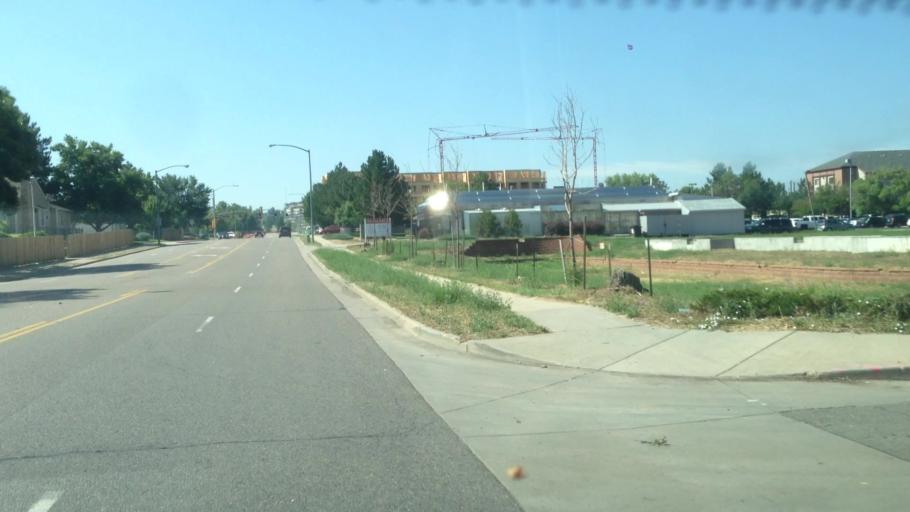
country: US
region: Colorado
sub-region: Adams County
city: Aurora
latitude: 39.6772
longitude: -104.8241
